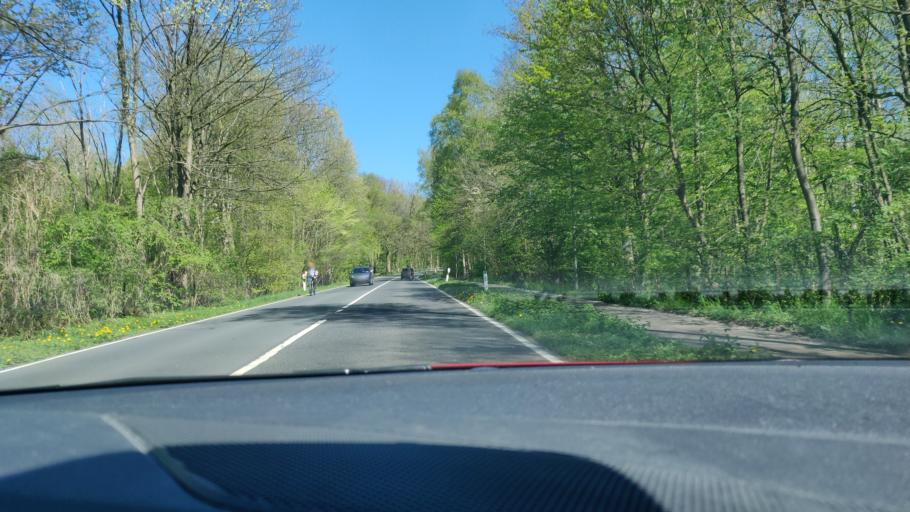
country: DE
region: North Rhine-Westphalia
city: Wulfrath
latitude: 51.2563
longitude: 7.0725
